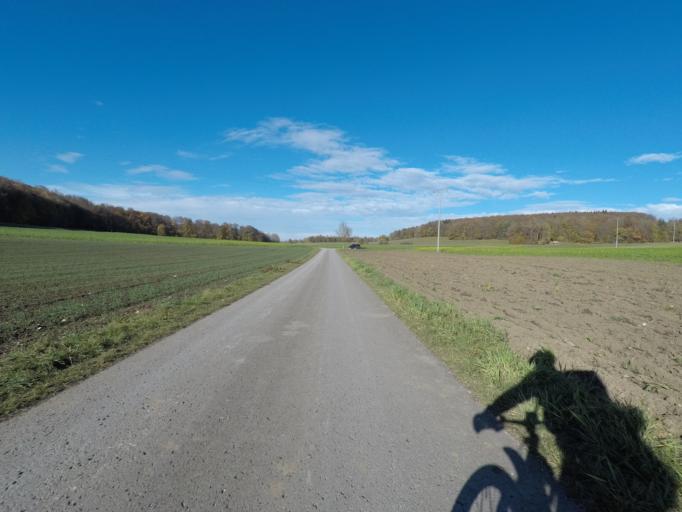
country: DE
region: Baden-Wuerttemberg
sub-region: Tuebingen Region
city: Pfullingen
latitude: 48.4148
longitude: 9.2116
